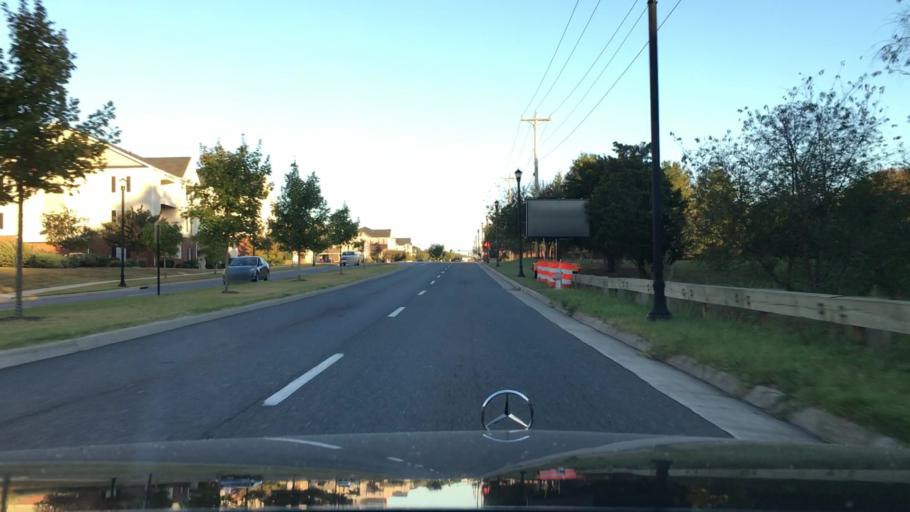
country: US
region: Virginia
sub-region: Campbell County
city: Timberlake
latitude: 37.3410
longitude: -79.2292
